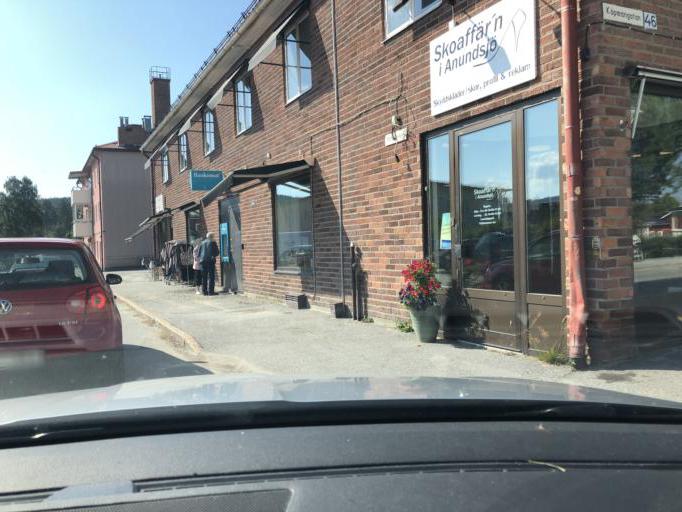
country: SE
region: Vaesternorrland
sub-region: OErnskoeldsviks Kommun
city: Bredbyn
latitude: 63.4484
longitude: 18.1093
